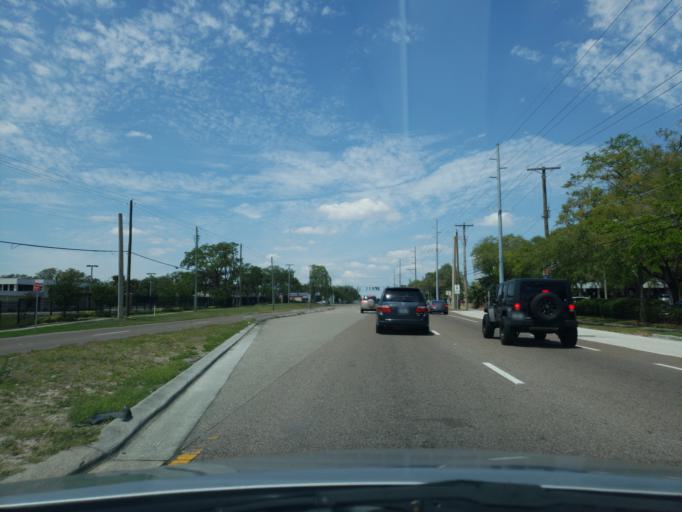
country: US
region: Florida
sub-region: Hillsborough County
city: University
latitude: 28.0692
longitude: -82.4238
